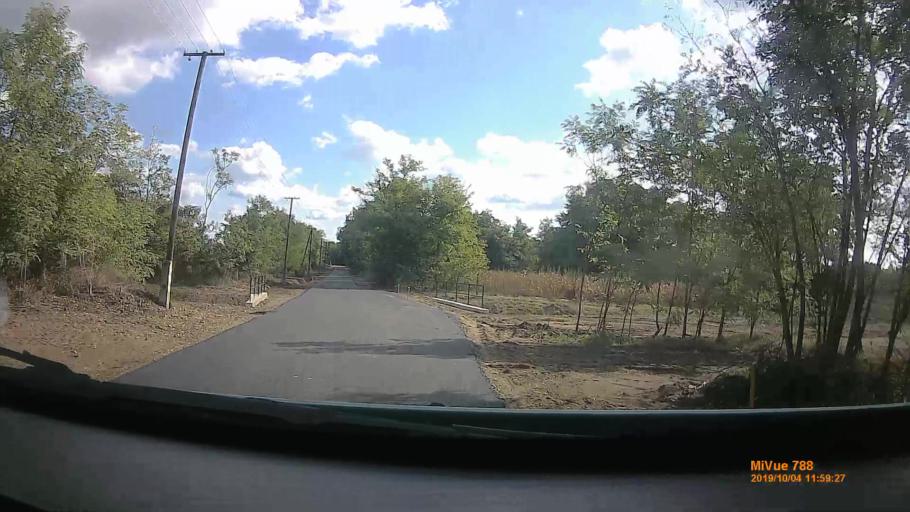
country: HU
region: Szabolcs-Szatmar-Bereg
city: Nyirtelek
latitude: 48.0162
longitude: 21.6723
